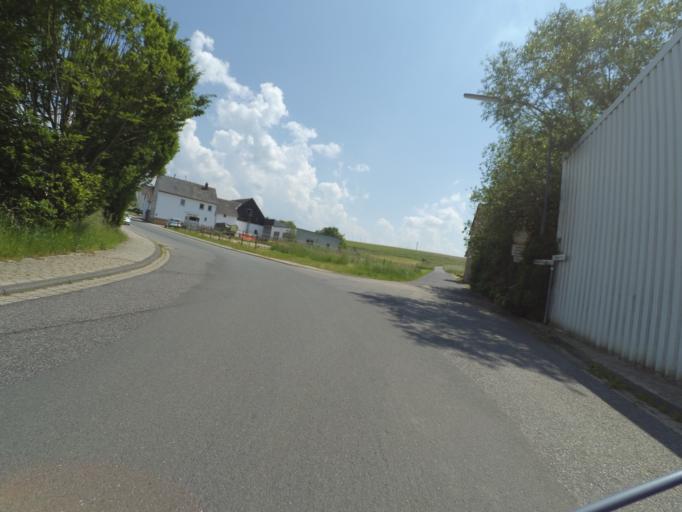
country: DE
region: Rheinland-Pfalz
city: Dunfus
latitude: 50.2196
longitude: 7.2347
